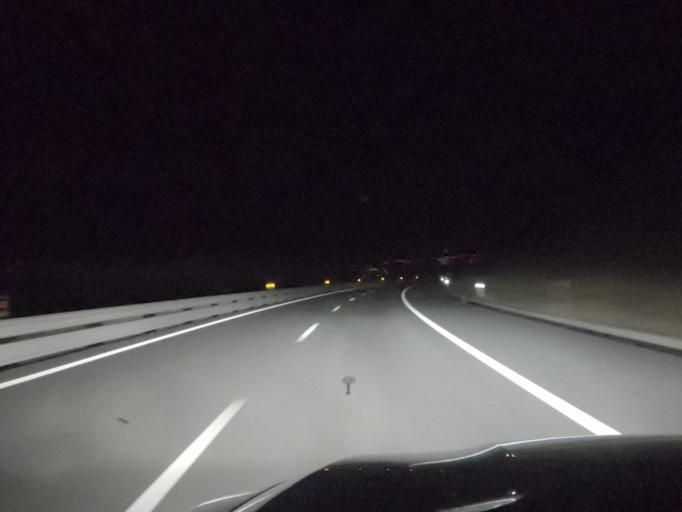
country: PT
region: Vila Real
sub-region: Santa Marta de Penaguiao
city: Santa Marta de Penaguiao
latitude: 41.2760
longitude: -7.8240
